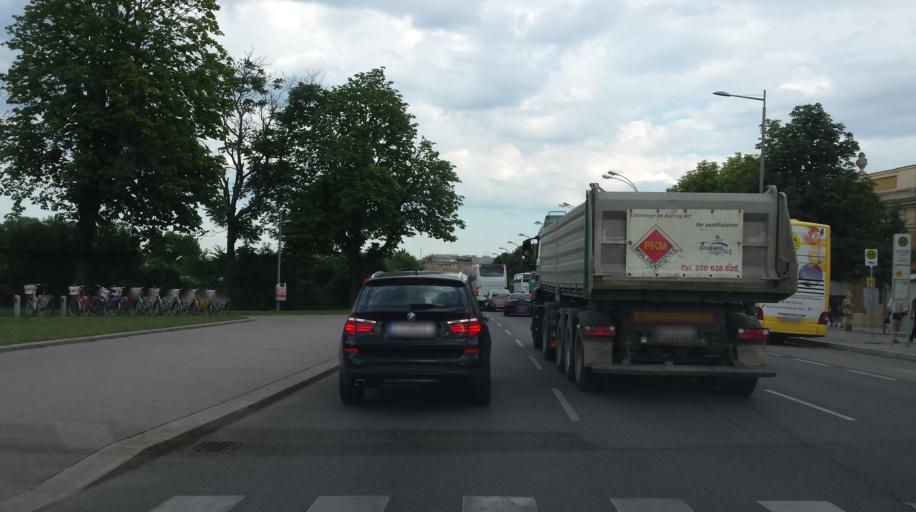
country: AT
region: Vienna
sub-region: Wien Stadt
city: Vienna
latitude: 48.1868
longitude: 16.3139
